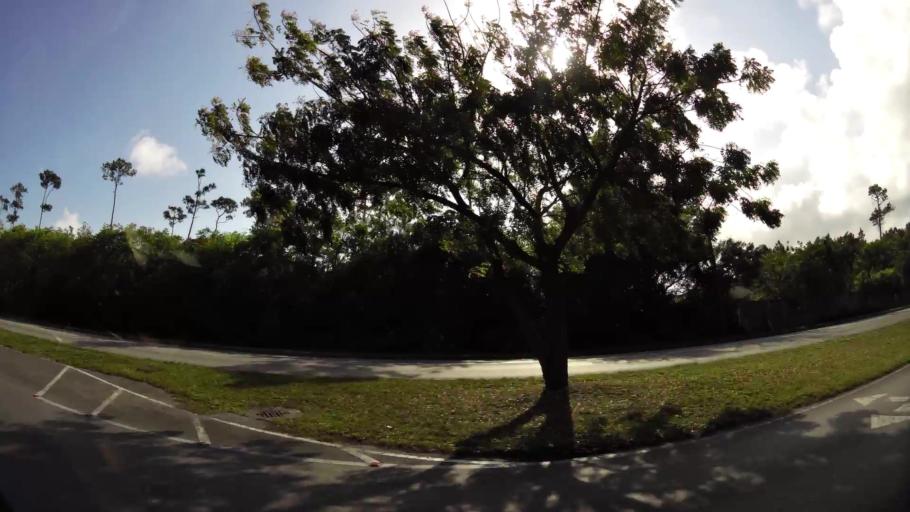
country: BS
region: Freeport
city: Lucaya
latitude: 26.5234
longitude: -78.6716
